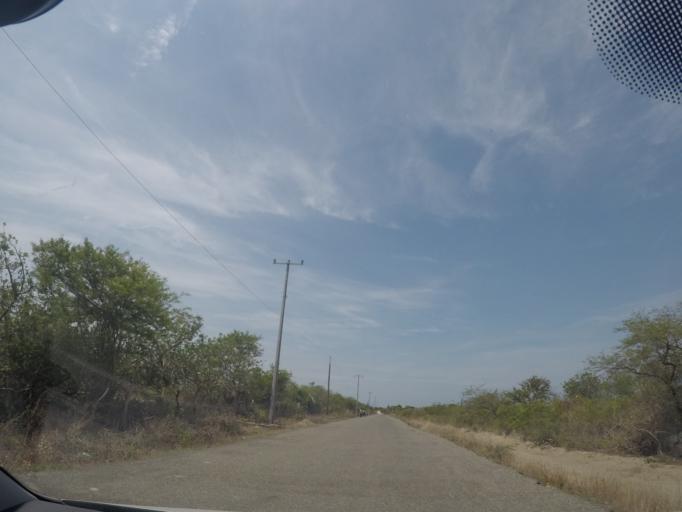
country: MX
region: Oaxaca
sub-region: Salina Cruz
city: Salina Cruz
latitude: 16.1956
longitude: -95.1194
